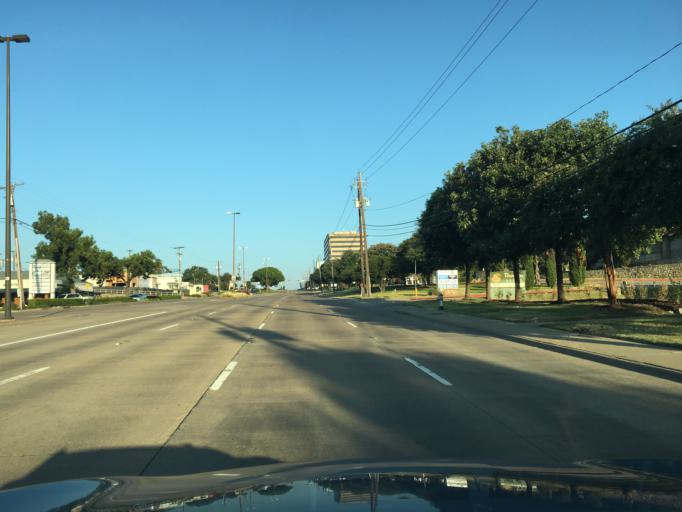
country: US
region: Texas
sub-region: Dallas County
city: Addison
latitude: 32.9541
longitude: -96.8148
